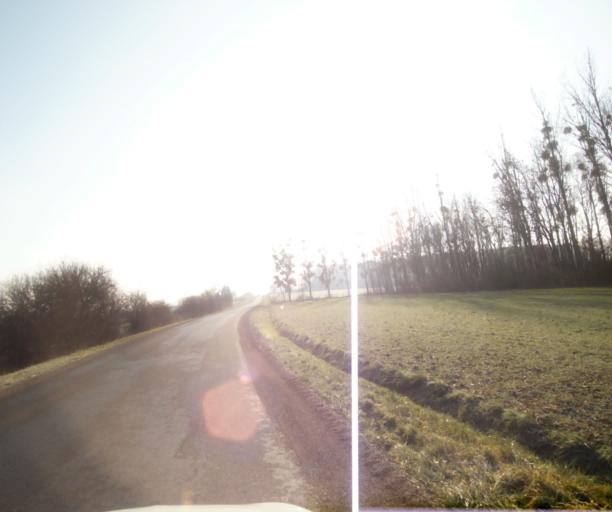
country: FR
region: Champagne-Ardenne
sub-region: Departement de la Haute-Marne
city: Montier-en-Der
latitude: 48.4910
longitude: 4.7346
